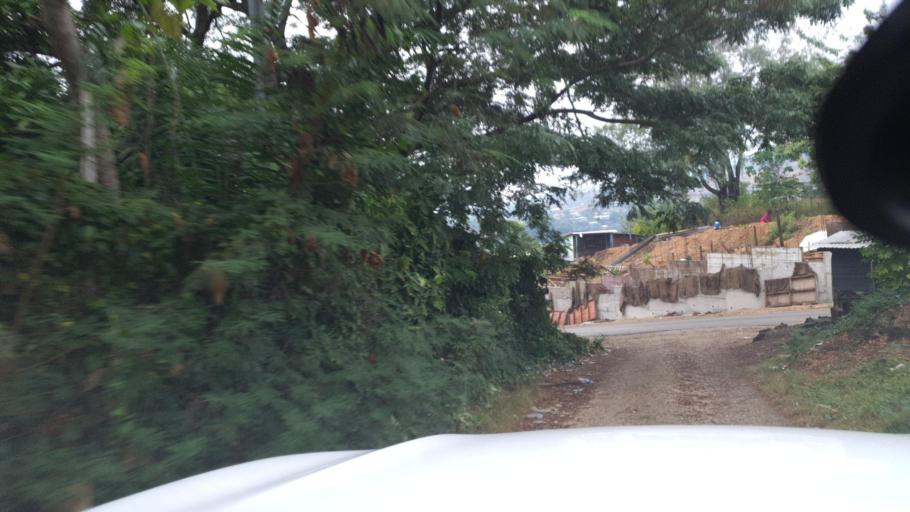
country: SB
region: Guadalcanal
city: Honiara
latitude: -9.4438
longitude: 159.9687
